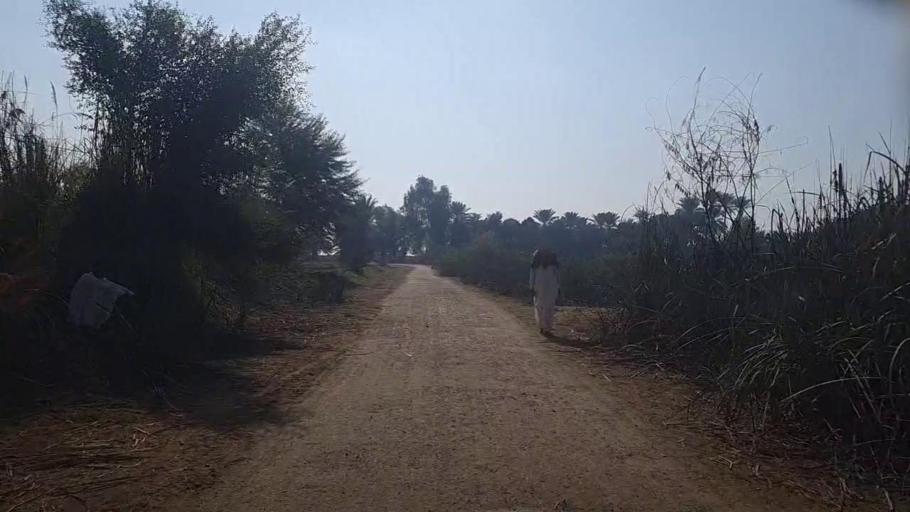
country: PK
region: Sindh
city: Kot Diji
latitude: 27.4233
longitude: 68.7373
